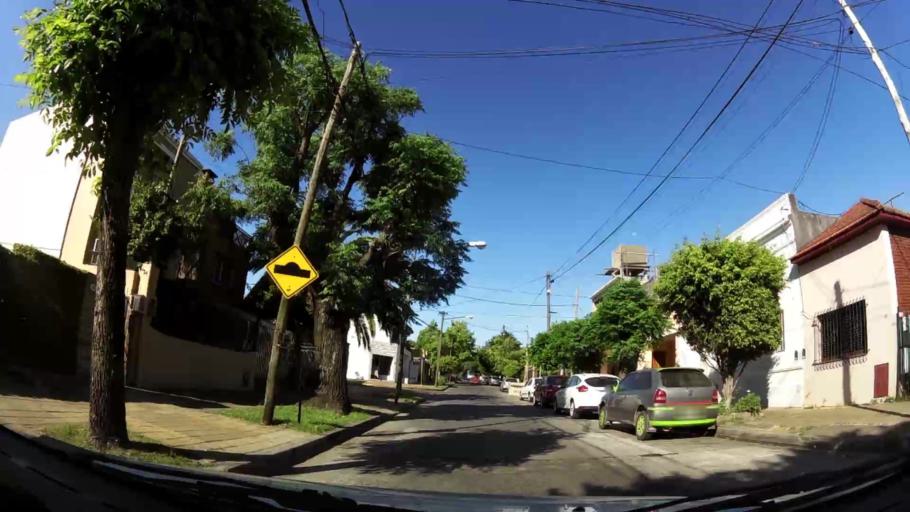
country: AR
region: Buenos Aires
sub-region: Partido de San Isidro
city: San Isidro
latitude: -34.4763
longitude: -58.5277
